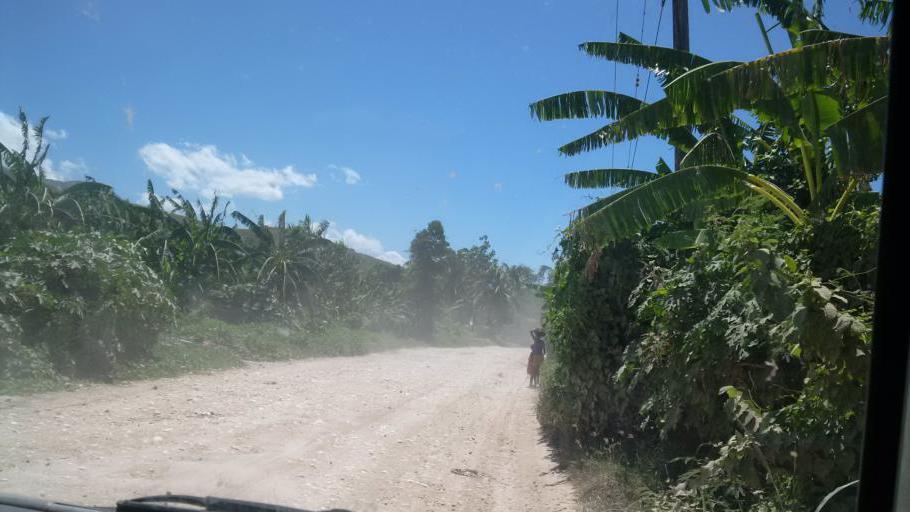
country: HT
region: Ouest
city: Thomazeau
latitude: 18.6571
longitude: -72.1388
